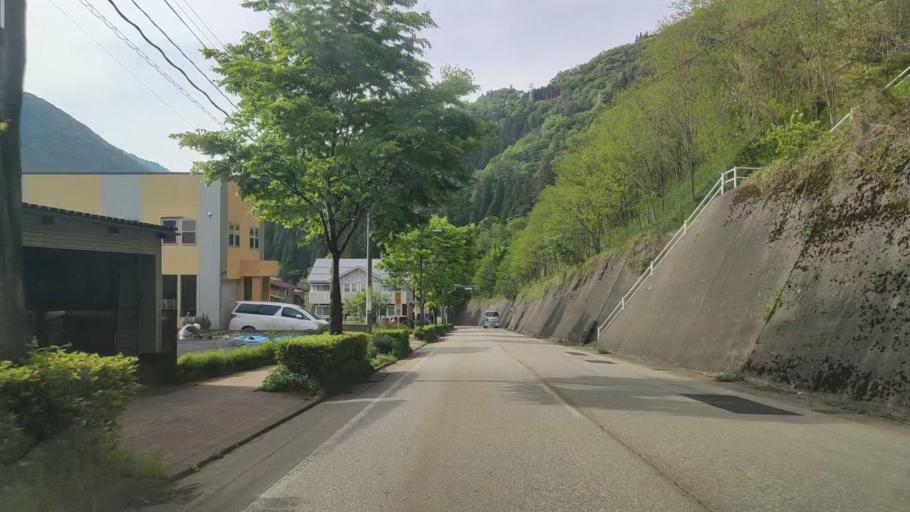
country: JP
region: Gifu
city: Takayama
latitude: 36.3323
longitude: 137.3046
